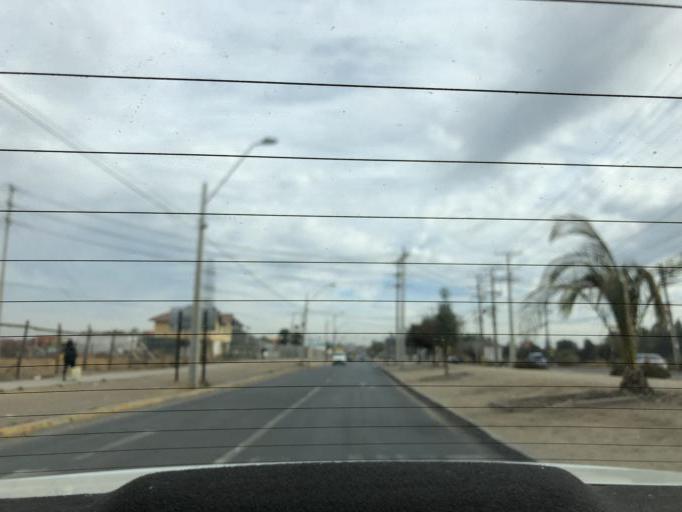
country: CL
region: Santiago Metropolitan
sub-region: Provincia de Cordillera
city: Puente Alto
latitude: -33.6114
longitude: -70.5438
